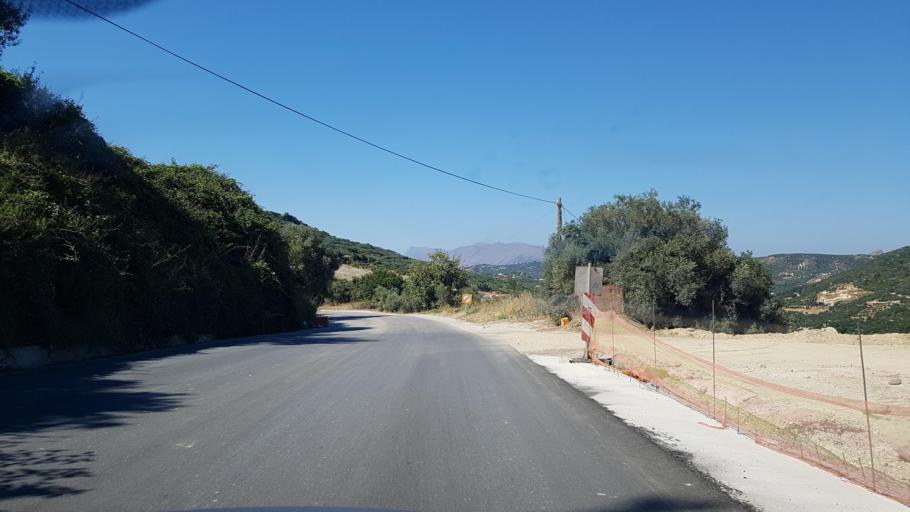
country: GR
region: Crete
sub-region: Nomos Chanias
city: Kissamos
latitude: 35.4312
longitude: 23.6869
